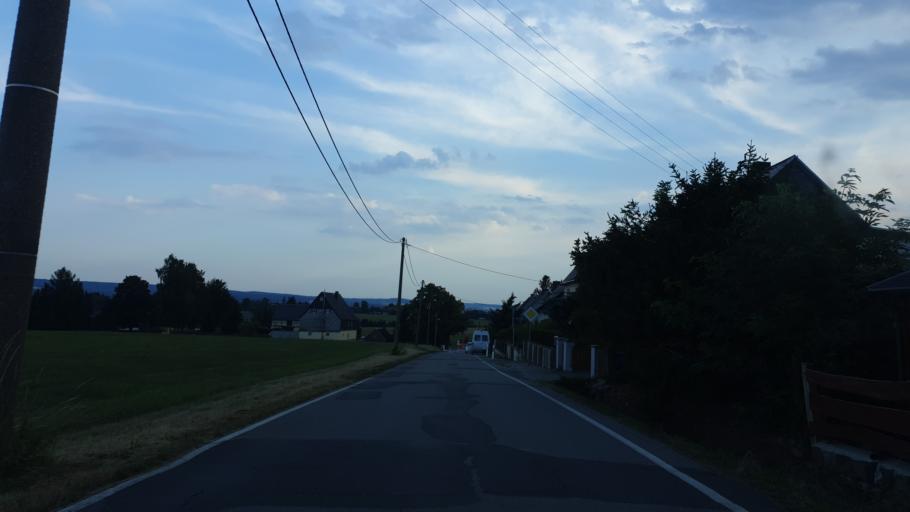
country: DE
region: Saxony
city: Niederdorf
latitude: 50.7795
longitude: 12.8045
